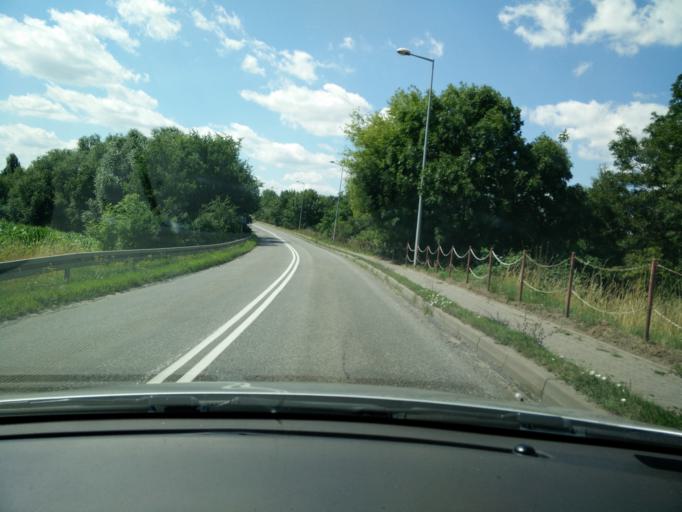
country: PL
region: Greater Poland Voivodeship
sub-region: Powiat sredzki
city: Sroda Wielkopolska
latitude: 52.2313
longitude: 17.2949
